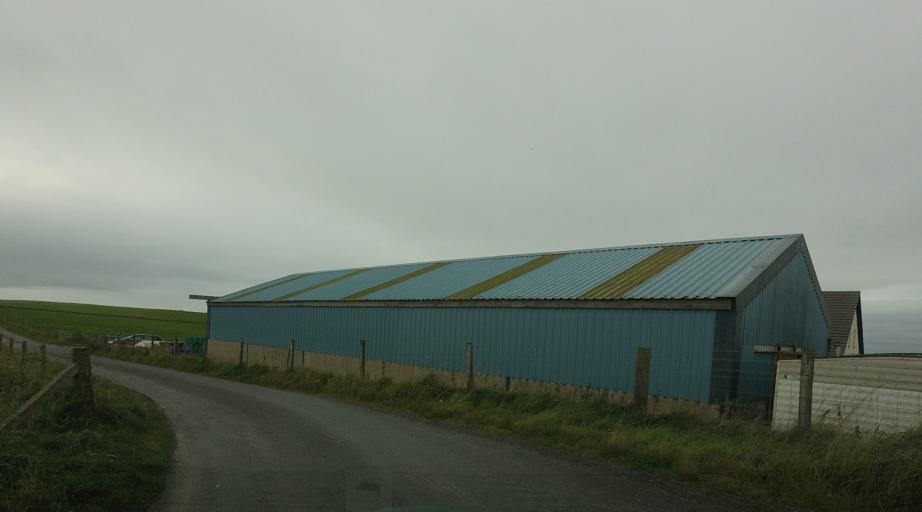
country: GB
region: Scotland
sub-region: Orkney Islands
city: Orkney
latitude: 58.8014
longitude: -2.9453
